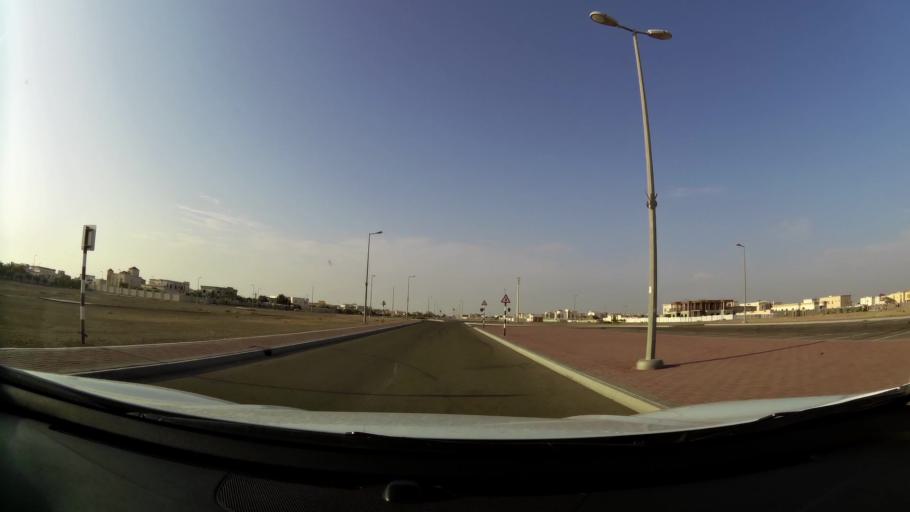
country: AE
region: Abu Dhabi
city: Al Ain
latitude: 24.0994
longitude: 55.8353
